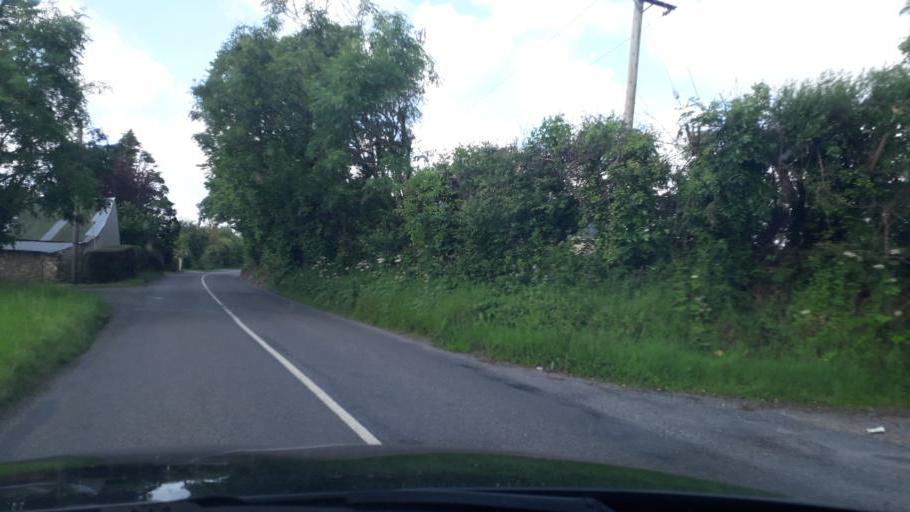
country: IE
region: Leinster
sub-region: Loch Garman
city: Loch Garman
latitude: 52.2828
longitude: -6.5382
